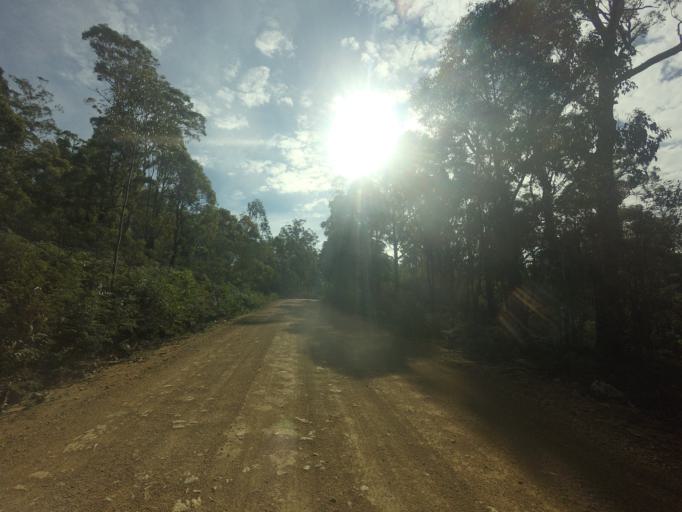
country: AU
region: Tasmania
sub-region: Sorell
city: Sorell
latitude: -42.5555
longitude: 147.4575
